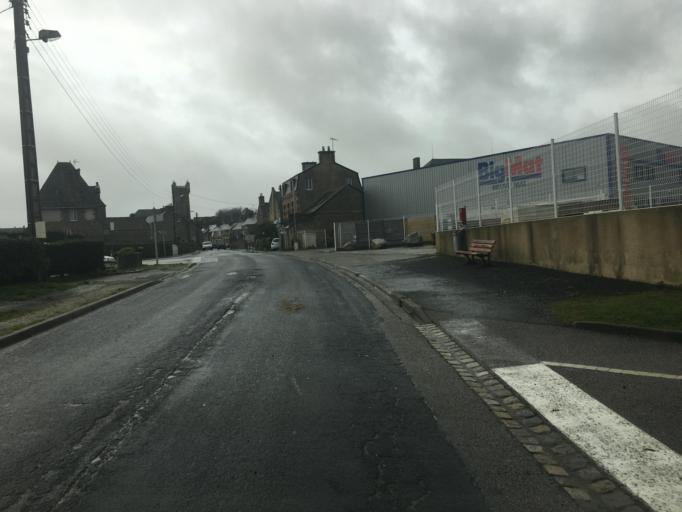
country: FR
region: Lower Normandy
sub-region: Departement de la Manche
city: Saint-Pierre-Eglise
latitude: 49.6716
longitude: -1.4042
